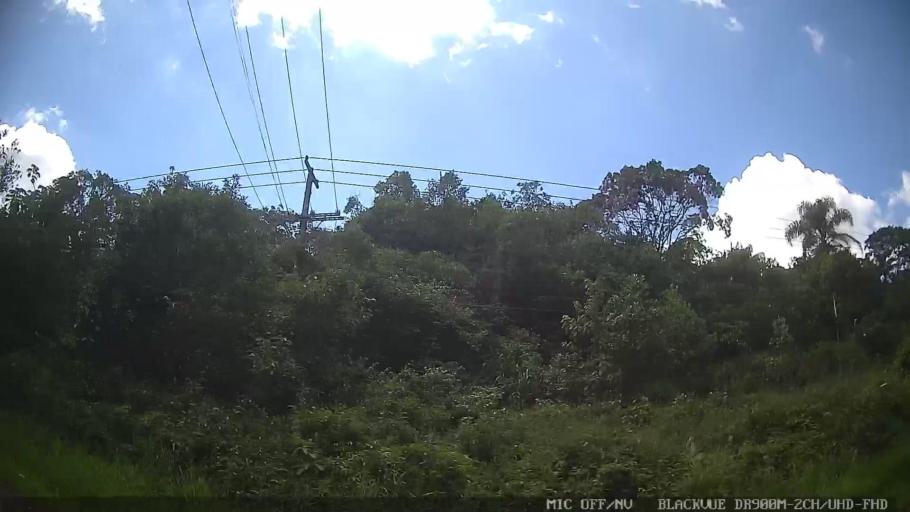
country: BR
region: Sao Paulo
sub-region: Mogi das Cruzes
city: Mogi das Cruzes
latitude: -23.6534
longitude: -46.1992
